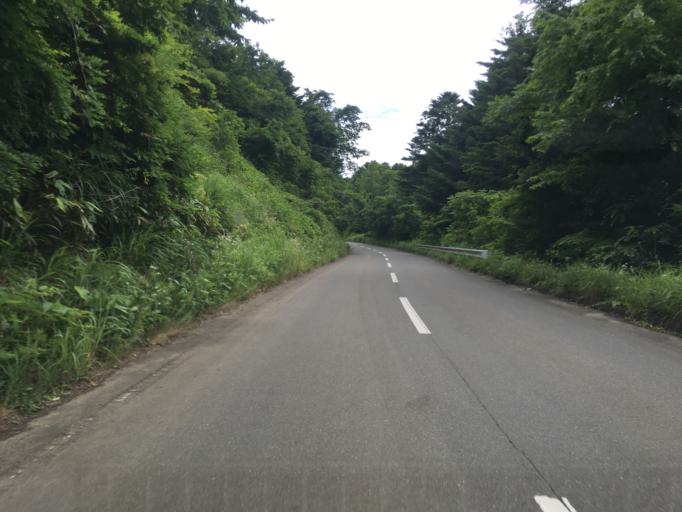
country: JP
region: Fukushima
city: Namie
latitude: 37.6940
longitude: 140.8837
